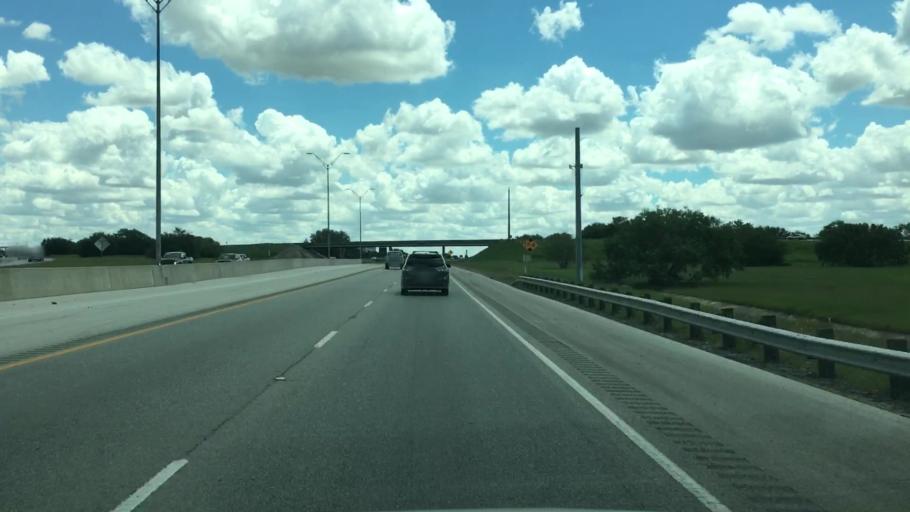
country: US
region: Texas
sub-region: Bexar County
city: Elmendorf
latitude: 29.3096
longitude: -98.4017
